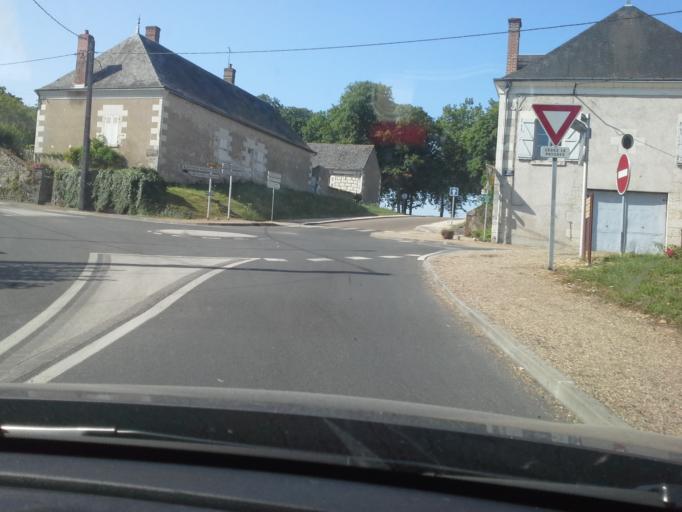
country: FR
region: Centre
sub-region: Departement du Loir-et-Cher
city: Chaumont-sur-Loire
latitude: 47.4761
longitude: 1.1897
